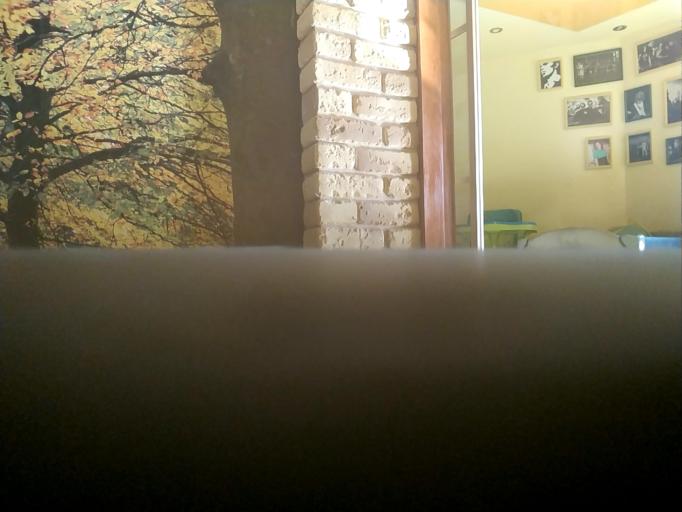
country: RU
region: Smolensk
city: Temkino
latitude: 54.9583
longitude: 34.9535
